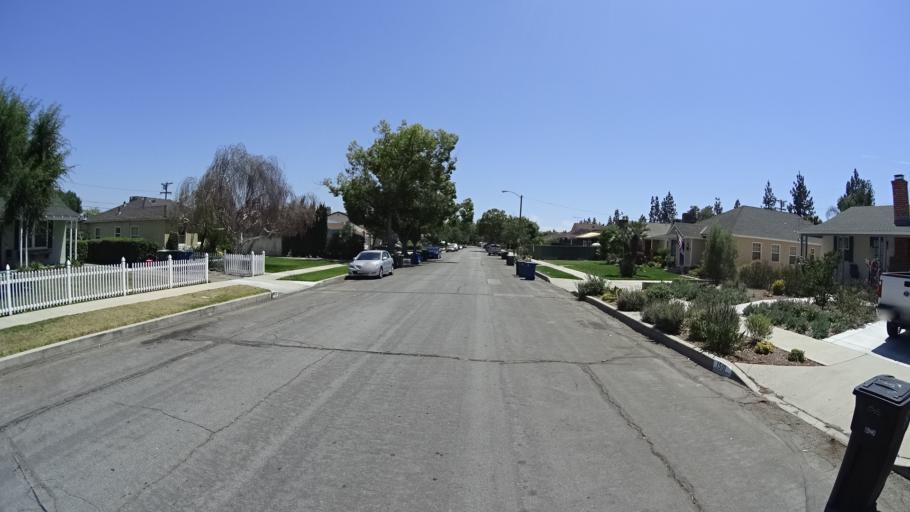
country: US
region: California
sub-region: Los Angeles County
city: Burbank
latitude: 34.1832
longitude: -118.3416
